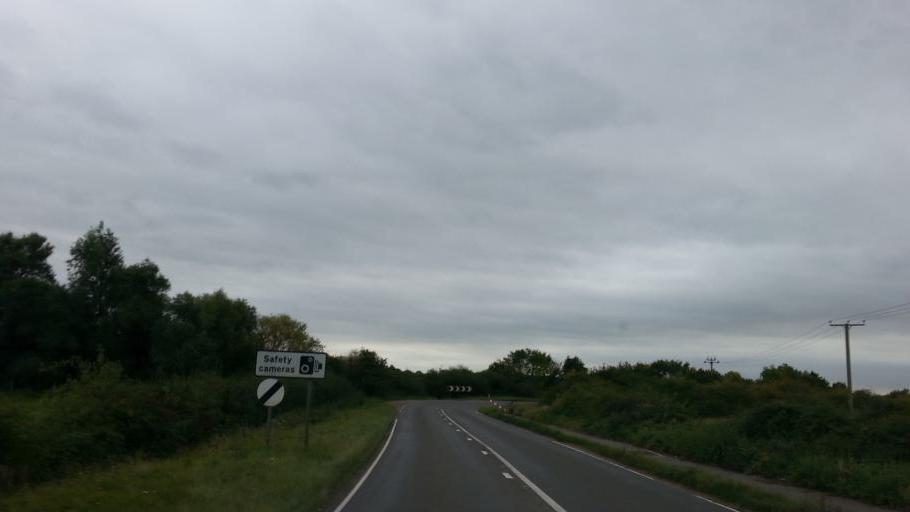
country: GB
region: England
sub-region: Cambridgeshire
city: Needingworth
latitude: 52.3447
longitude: -0.0022
